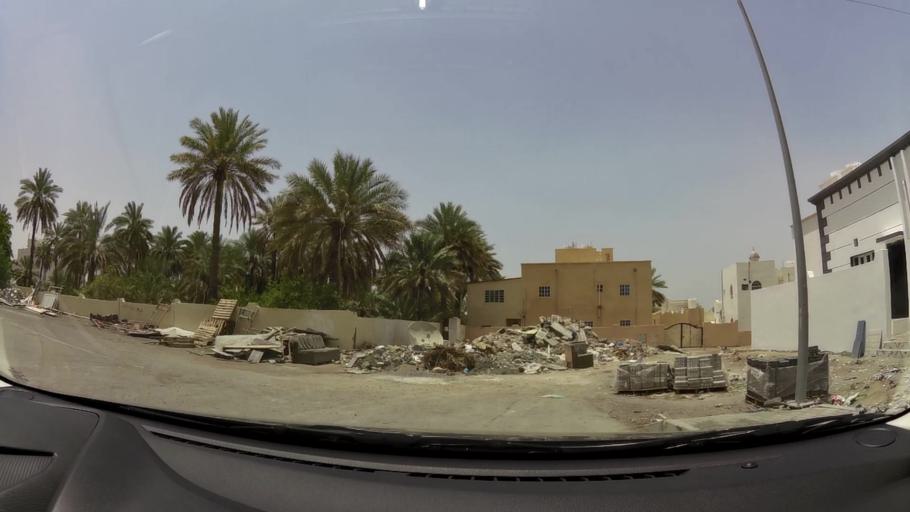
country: OM
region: Muhafazat Masqat
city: Bawshar
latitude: 23.5346
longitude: 58.3957
